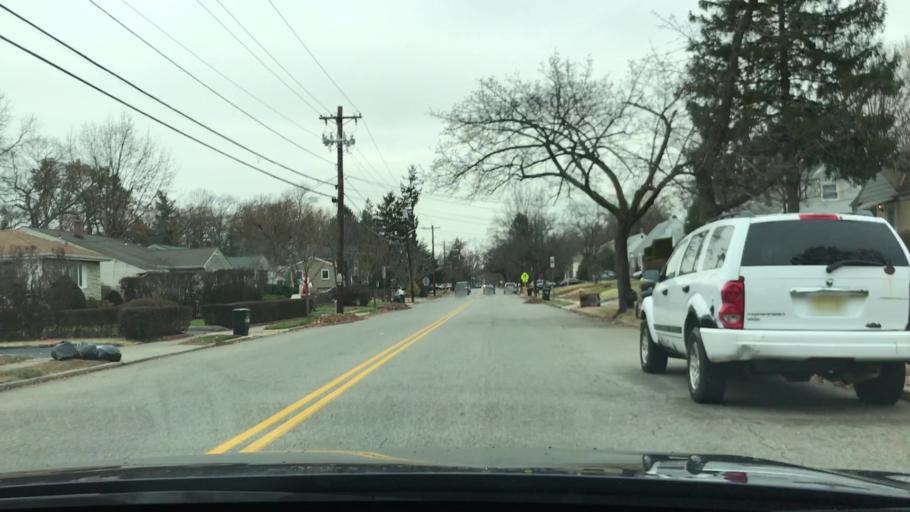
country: US
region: New Jersey
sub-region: Bergen County
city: New Milford
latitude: 40.9347
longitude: -74.0168
